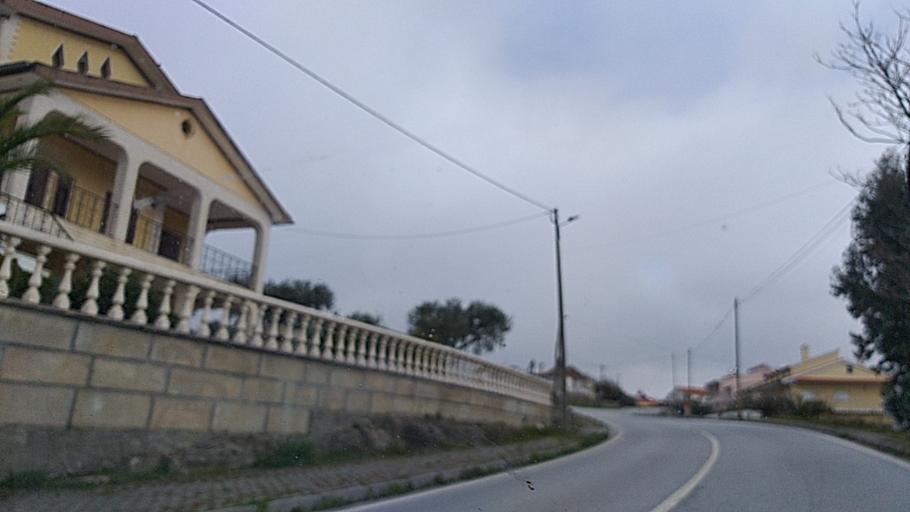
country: PT
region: Guarda
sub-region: Fornos de Algodres
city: Fornos de Algodres
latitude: 40.6807
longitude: -7.4709
